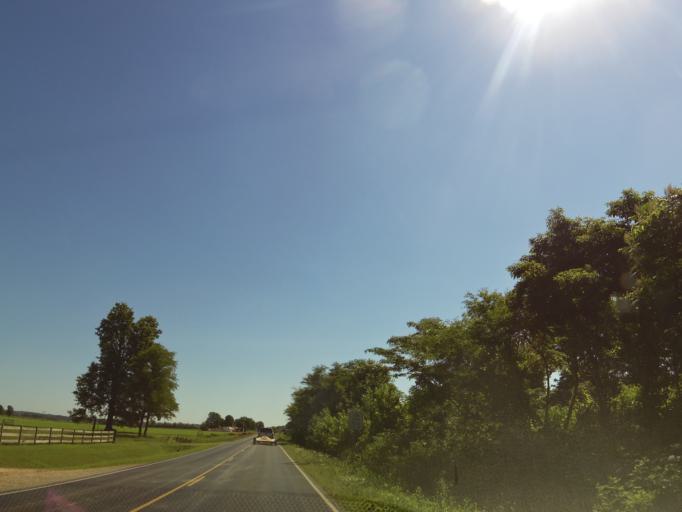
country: US
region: Missouri
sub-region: Dunklin County
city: Campbell
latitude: 36.4579
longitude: -90.1341
